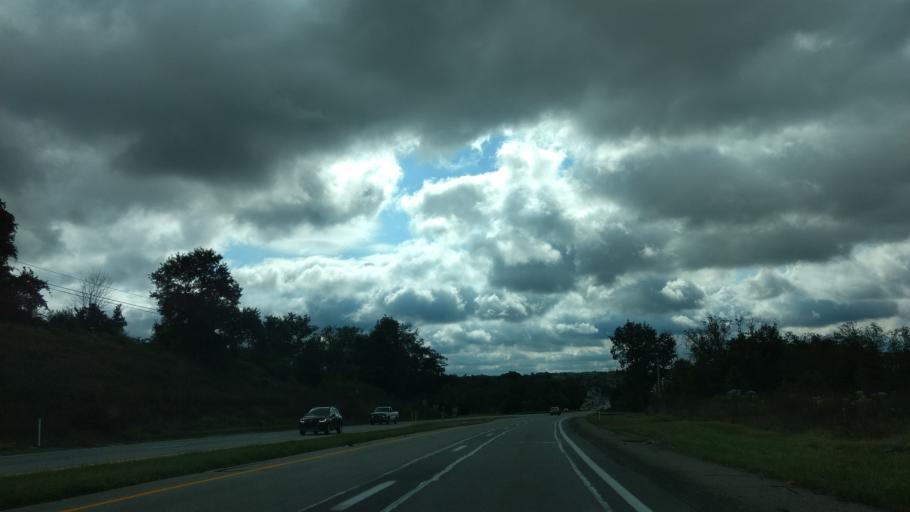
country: US
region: Pennsylvania
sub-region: Westmoreland County
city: Fellsburg
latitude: 40.1664
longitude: -79.7879
